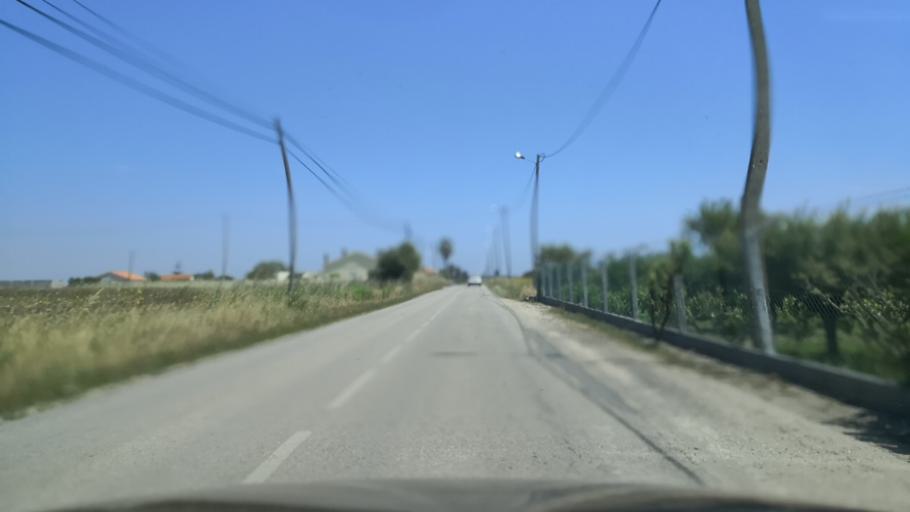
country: PT
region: Setubal
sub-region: Palmela
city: Palmela
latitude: 38.6015
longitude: -8.8023
